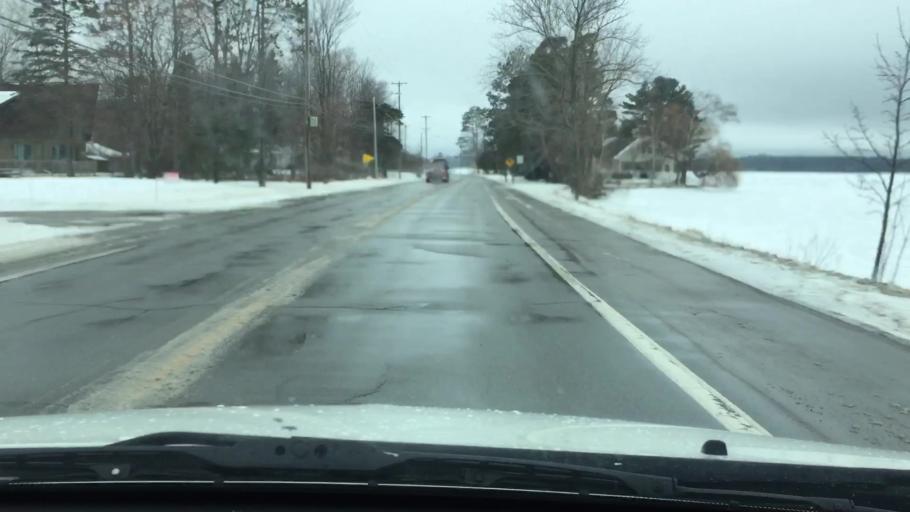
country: US
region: Michigan
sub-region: Wexford County
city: Cadillac
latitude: 44.2344
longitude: -85.4289
